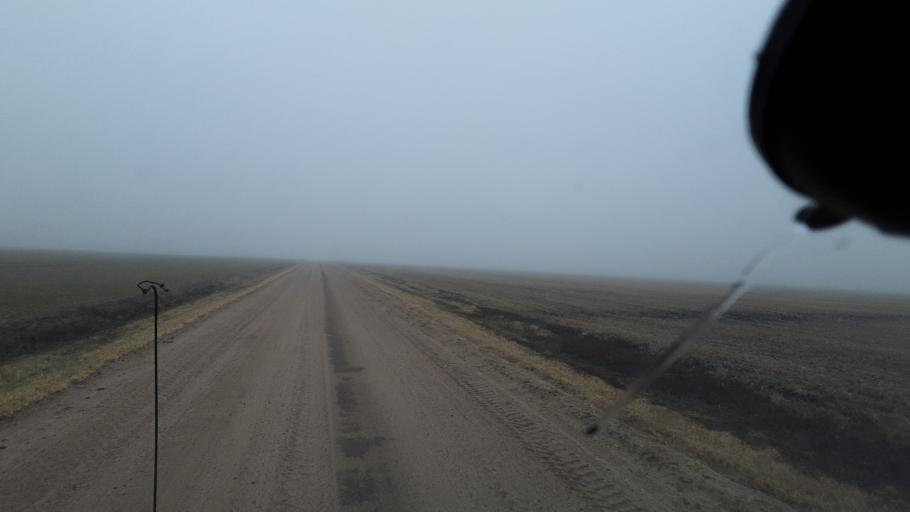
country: US
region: Kansas
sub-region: Reno County
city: South Hutchinson
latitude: 37.9665
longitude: -97.9956
